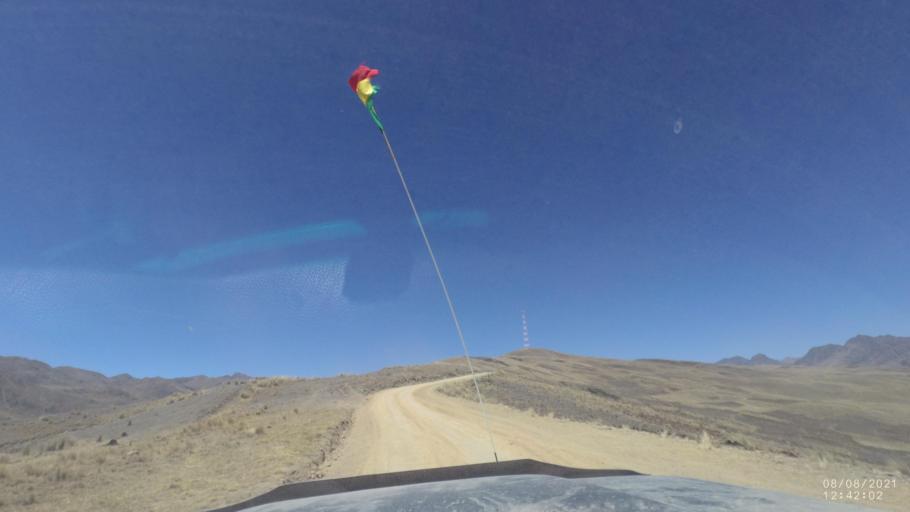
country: BO
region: Cochabamba
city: Colchani
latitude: -16.8373
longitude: -66.6177
